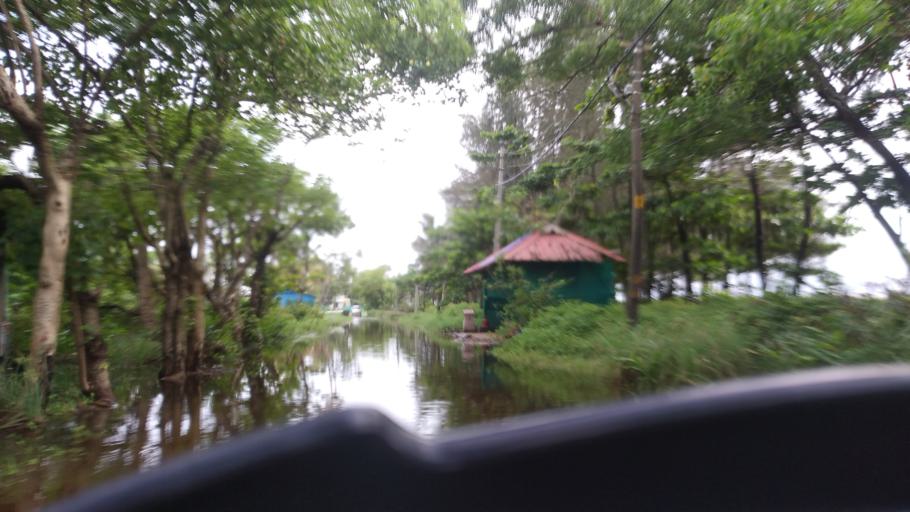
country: IN
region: Kerala
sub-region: Ernakulam
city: Elur
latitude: 10.1034
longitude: 76.1892
